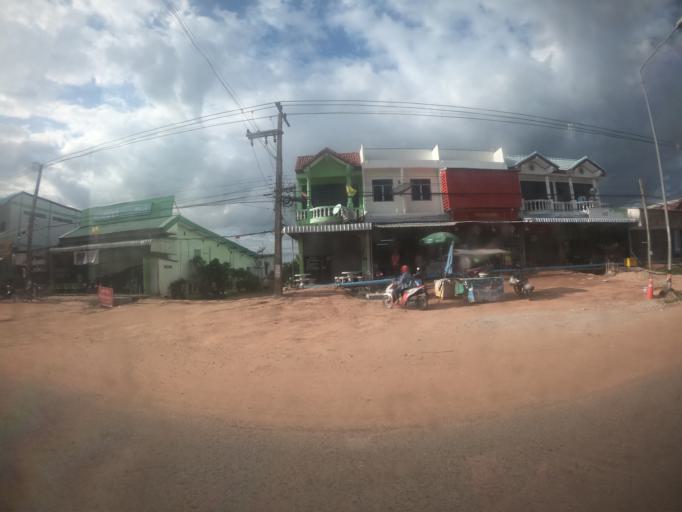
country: TH
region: Surin
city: Kap Choeng
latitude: 14.4756
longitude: 103.5958
